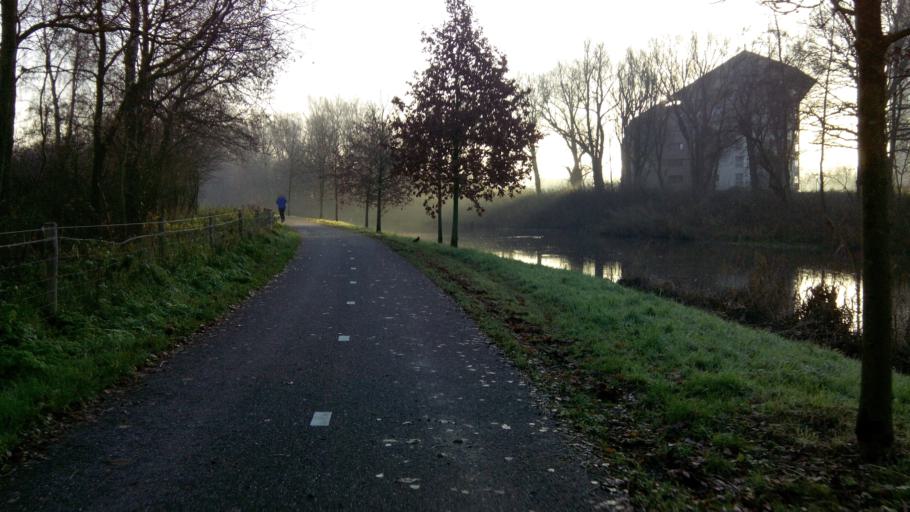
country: NL
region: Utrecht
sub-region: Gemeente Leusden
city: Leusden
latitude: 52.1429
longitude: 5.4359
